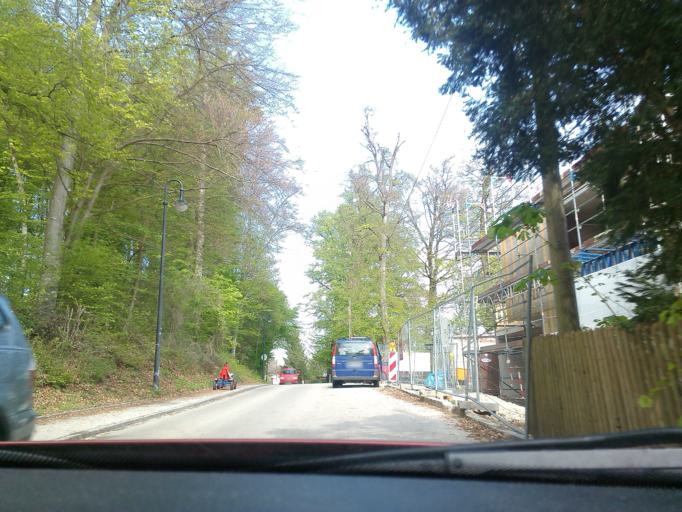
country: DE
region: Bavaria
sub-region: Upper Bavaria
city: Wessling
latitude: 48.0703
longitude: 11.2582
